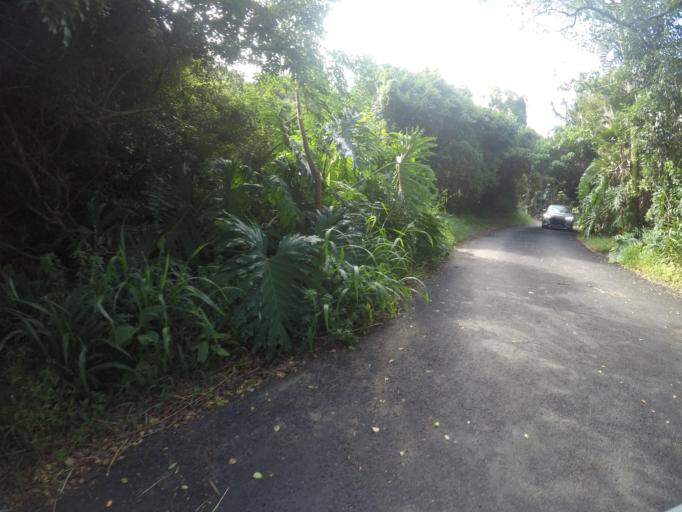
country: ZA
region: Eastern Cape
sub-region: Buffalo City Metropolitan Municipality
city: East London
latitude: -32.9678
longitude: 27.9576
